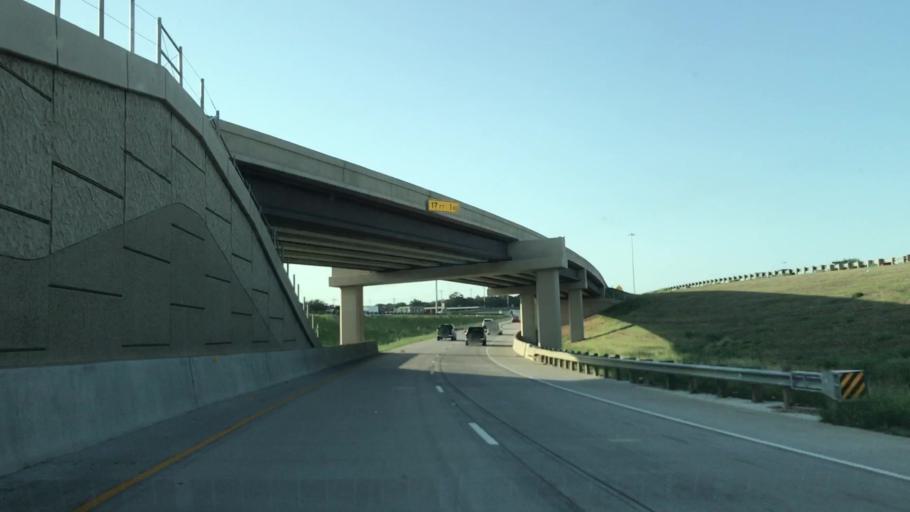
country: US
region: Texas
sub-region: Tarrant County
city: Grapevine
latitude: 32.9051
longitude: -97.0984
